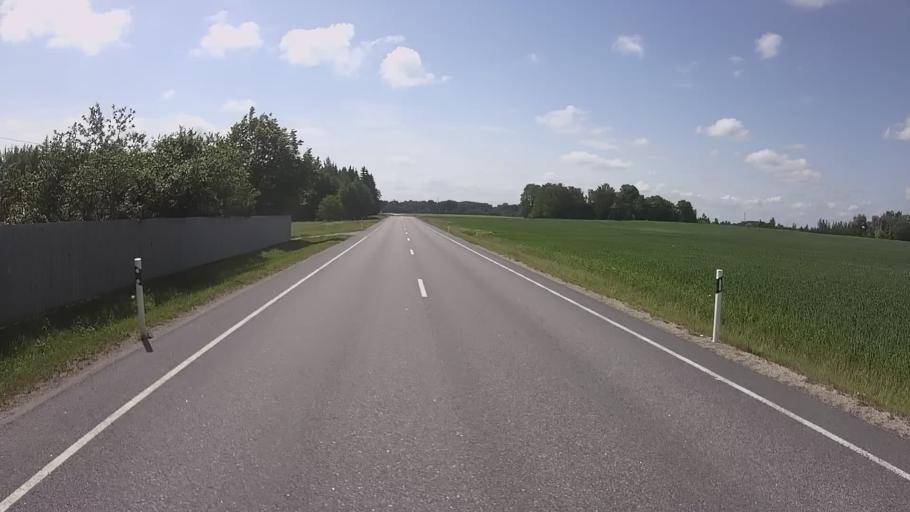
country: EE
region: Tartu
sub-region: Tartu linn
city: Tartu
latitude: 58.3816
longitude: 26.8868
